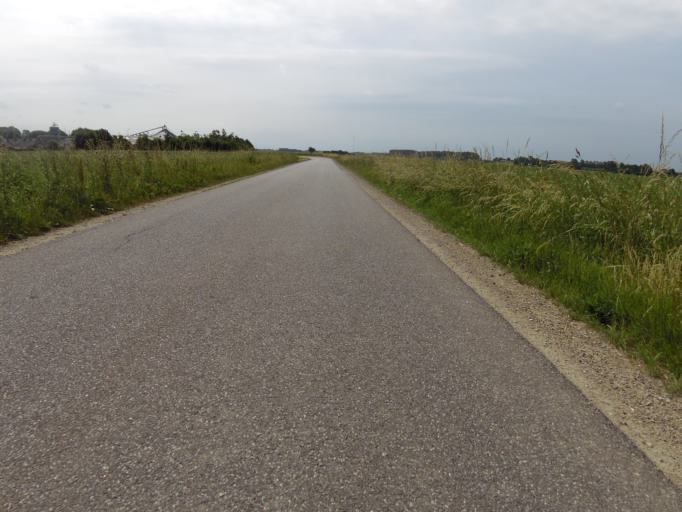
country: DK
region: Central Jutland
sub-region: Holstebro Kommune
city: Holstebro
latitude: 56.4288
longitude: 8.6400
